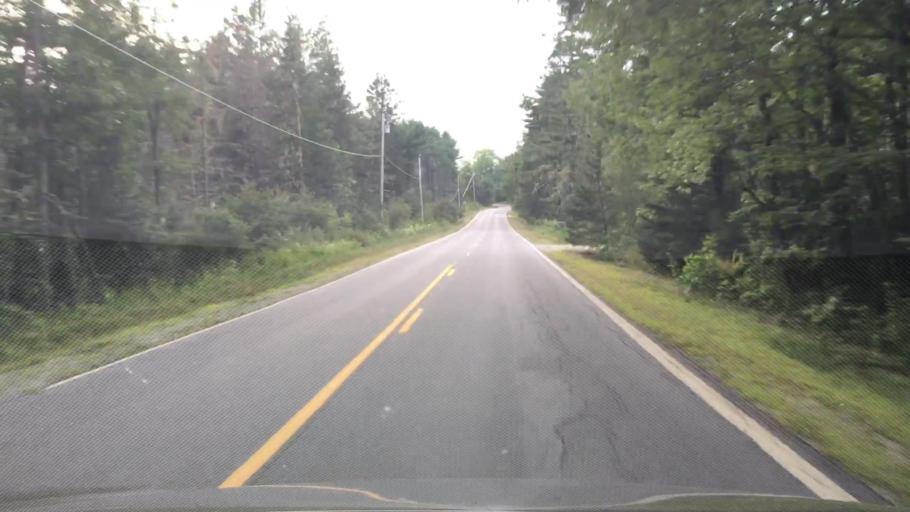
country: US
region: Maine
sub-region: Hancock County
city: Penobscot
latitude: 44.4508
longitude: -68.6965
